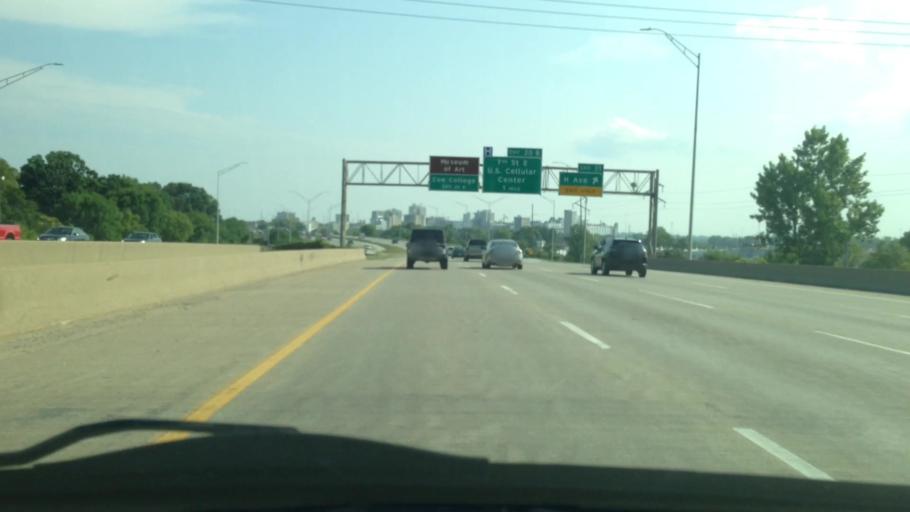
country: US
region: Iowa
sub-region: Linn County
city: Cedar Rapids
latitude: 42.0002
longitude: -91.6669
